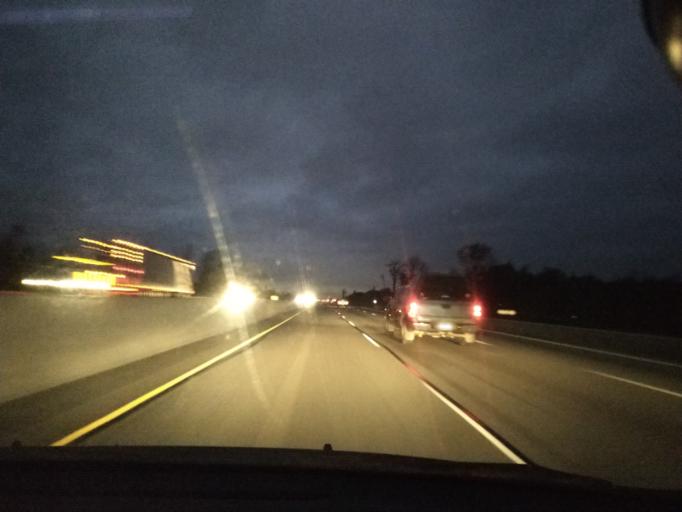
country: CA
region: Ontario
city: Innisfil
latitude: 44.2278
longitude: -79.6643
